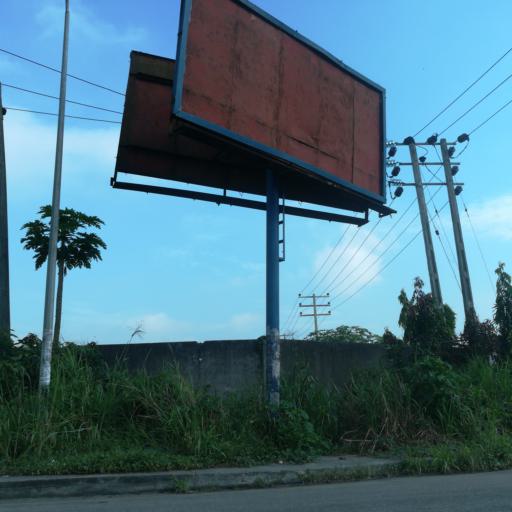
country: NG
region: Rivers
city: Port Harcourt
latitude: 4.8015
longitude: 7.0267
